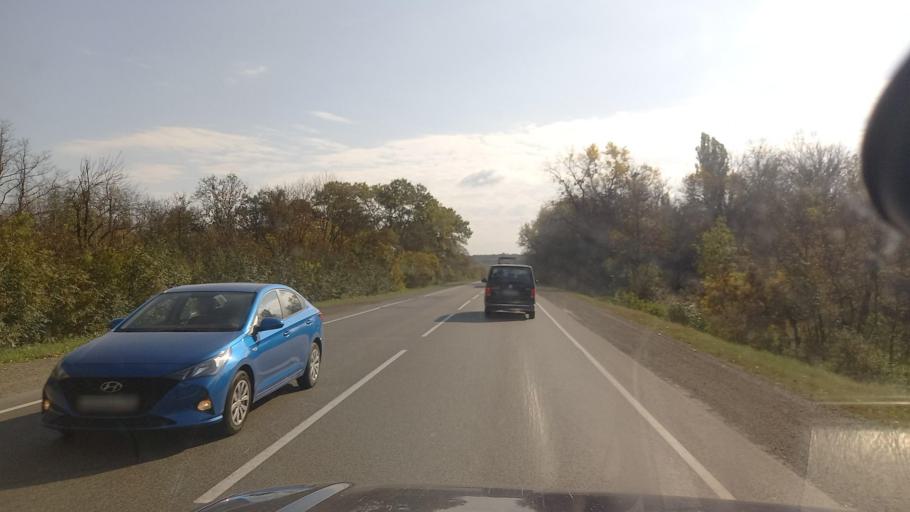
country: RU
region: Krasnodarskiy
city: Abinsk
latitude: 44.8429
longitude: 38.1570
